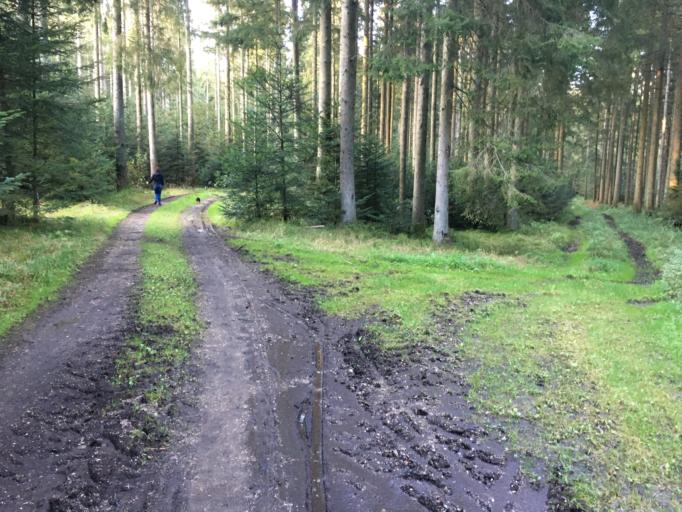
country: AT
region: Upper Austria
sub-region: Politischer Bezirk Vocklabruck
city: Frankenmarkt
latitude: 48.0065
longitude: 13.3997
